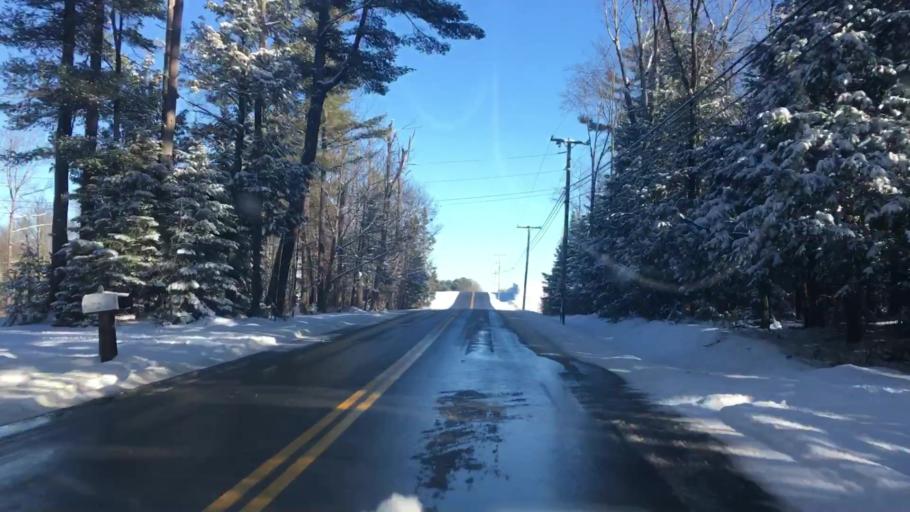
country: US
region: Maine
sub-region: Androscoggin County
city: Lisbon Falls
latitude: 43.9488
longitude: -70.1103
